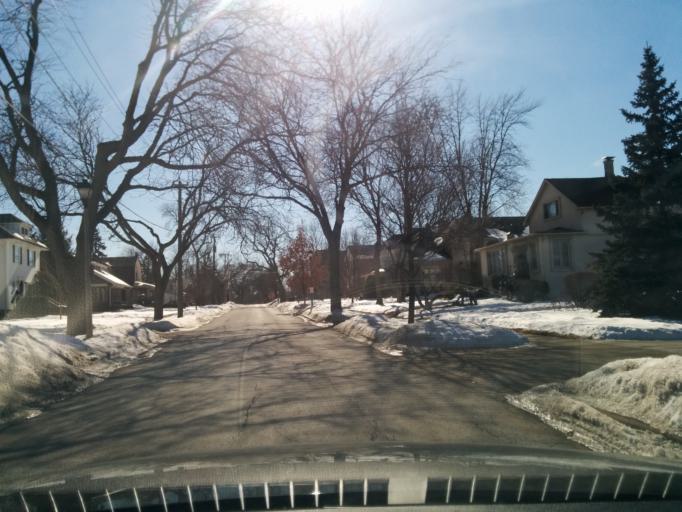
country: US
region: Illinois
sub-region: DuPage County
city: Elmhurst
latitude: 41.8986
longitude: -87.9368
